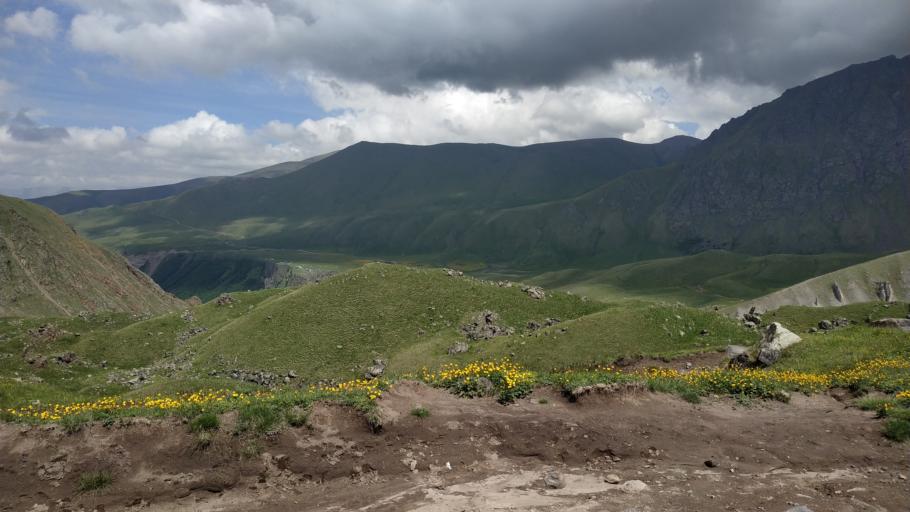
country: RU
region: Kabardino-Balkariya
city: Terskol
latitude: 43.4348
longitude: 42.5298
